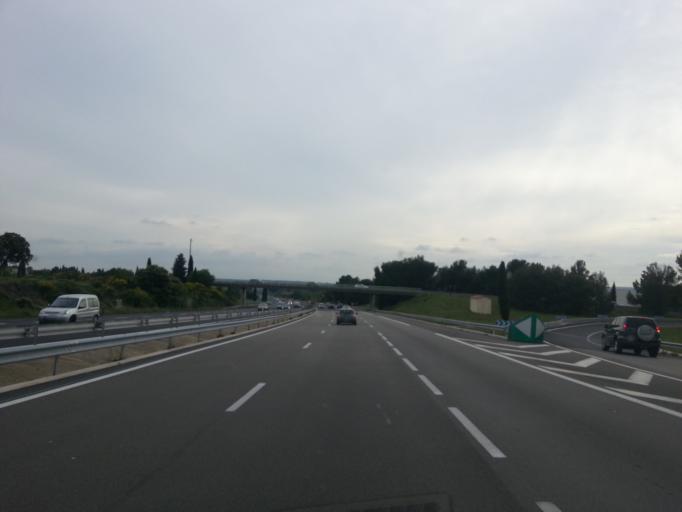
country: FR
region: Languedoc-Roussillon
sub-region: Departement du Gard
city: Remoulins
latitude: 43.9358
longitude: 4.6019
